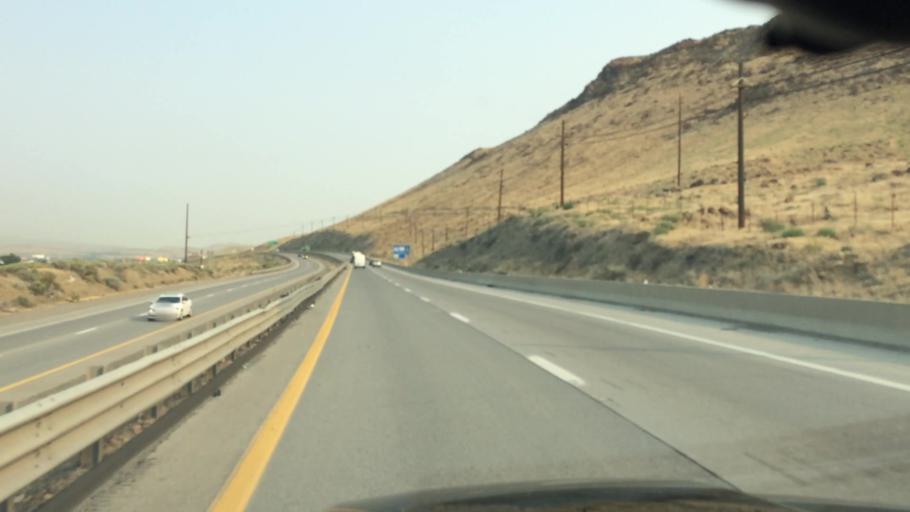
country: US
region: Nevada
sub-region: Washoe County
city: Sparks
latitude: 39.5195
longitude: -119.6851
